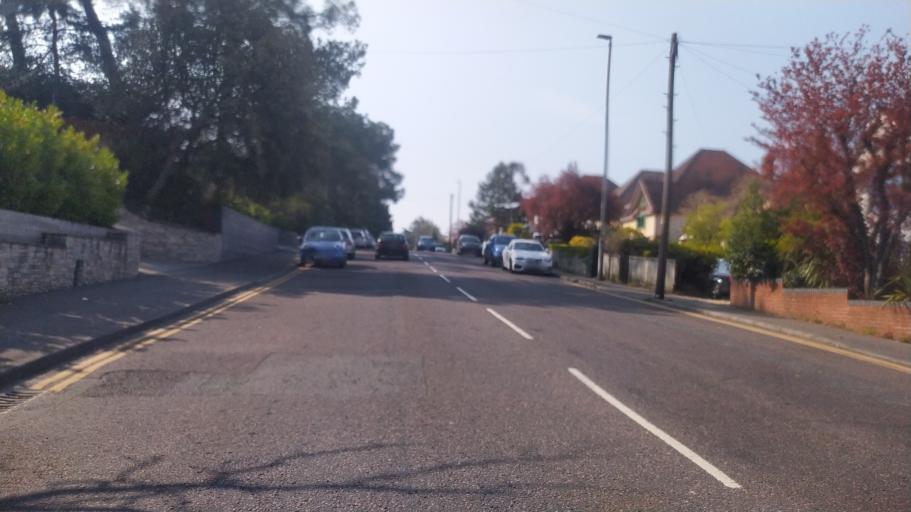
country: GB
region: England
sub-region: Dorset
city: Parkstone
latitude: 50.7226
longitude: -1.9252
